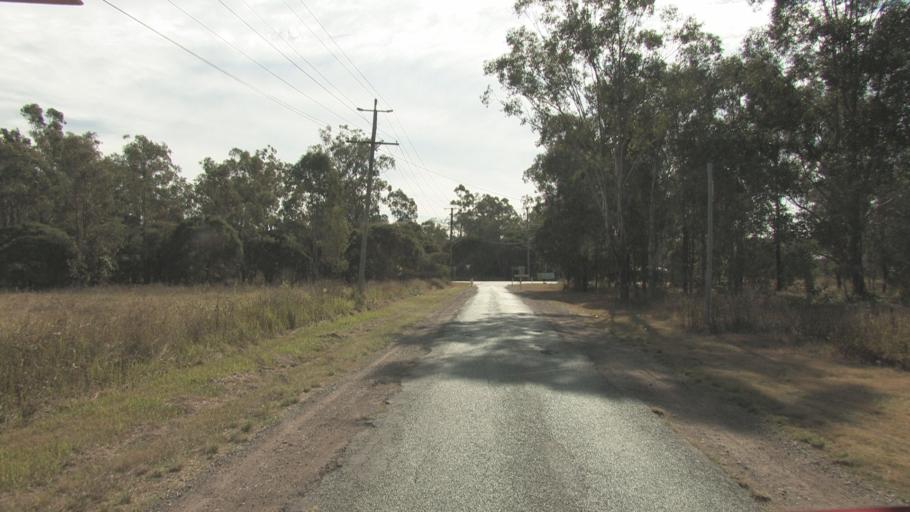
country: AU
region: Queensland
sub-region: Logan
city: North Maclean
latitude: -27.7757
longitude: 153.0085
